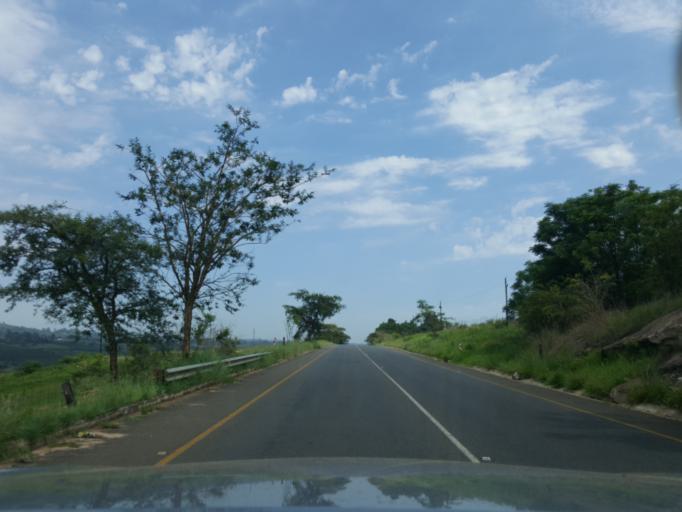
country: ZA
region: Mpumalanga
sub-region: Ehlanzeni District
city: White River
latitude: -25.3672
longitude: 31.0743
